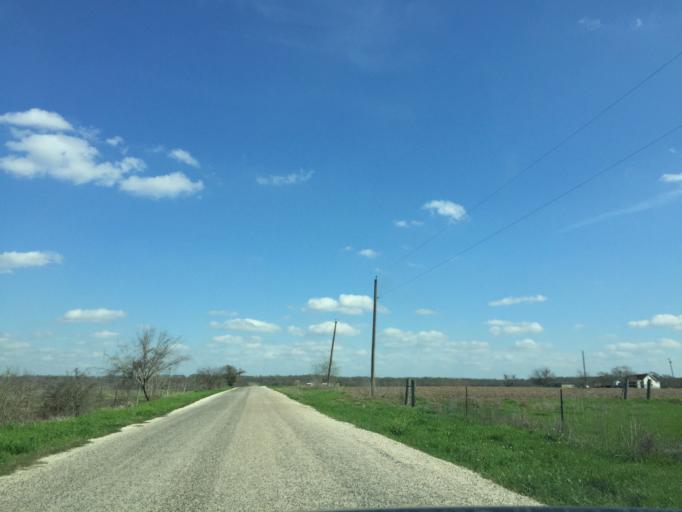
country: US
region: Texas
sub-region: Milam County
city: Thorndale
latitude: 30.5974
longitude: -97.1714
